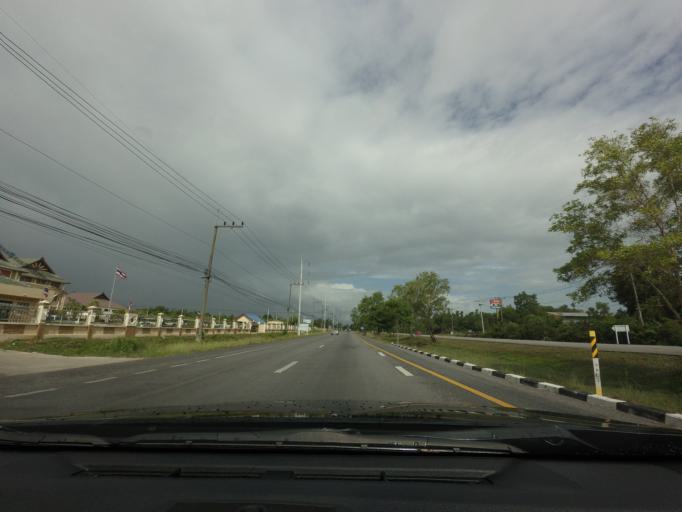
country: TH
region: Pattani
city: Nong Chik
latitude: 6.8093
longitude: 101.1119
